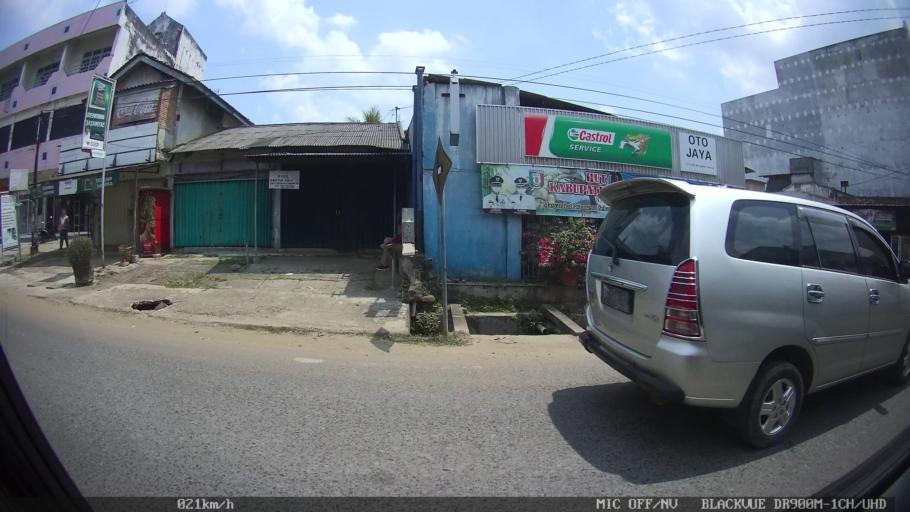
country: ID
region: Lampung
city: Pringsewu
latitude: -5.3557
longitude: 104.9781
